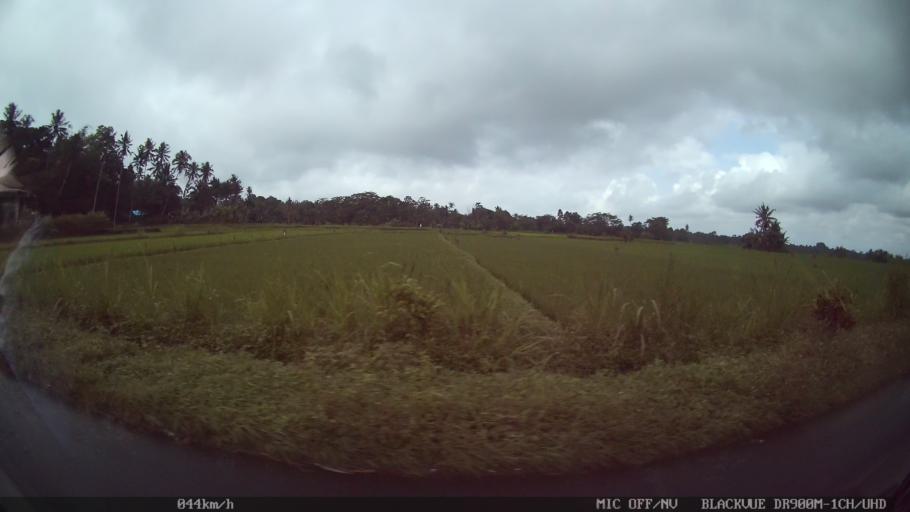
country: ID
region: Bali
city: Pegongan
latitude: -8.4938
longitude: 115.2259
